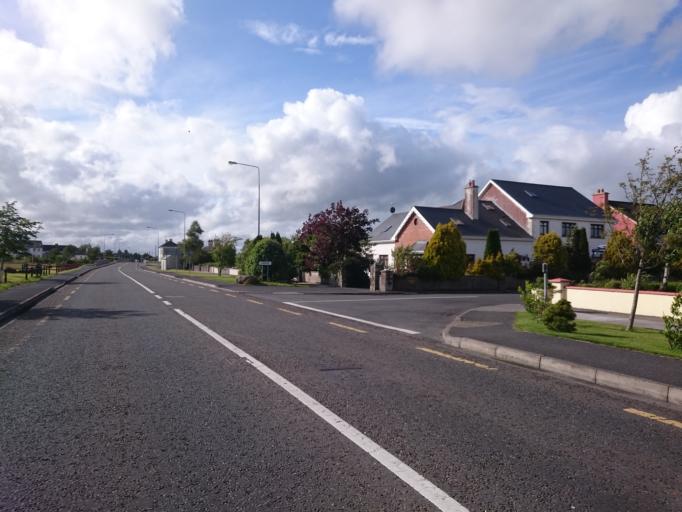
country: IE
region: Connaught
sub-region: Maigh Eo
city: Kiltamagh
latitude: 53.7967
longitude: -8.9217
